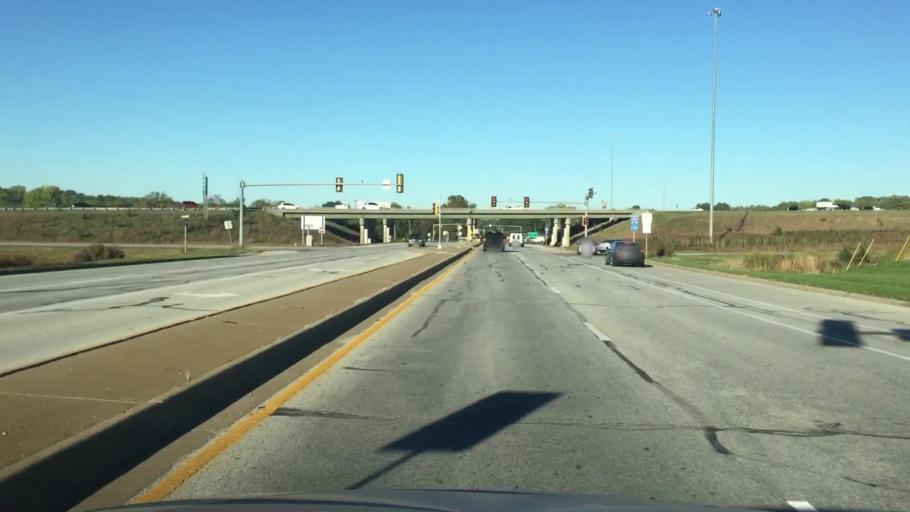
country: US
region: Kansas
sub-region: Johnson County
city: Lenexa
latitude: 38.9997
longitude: -94.7801
